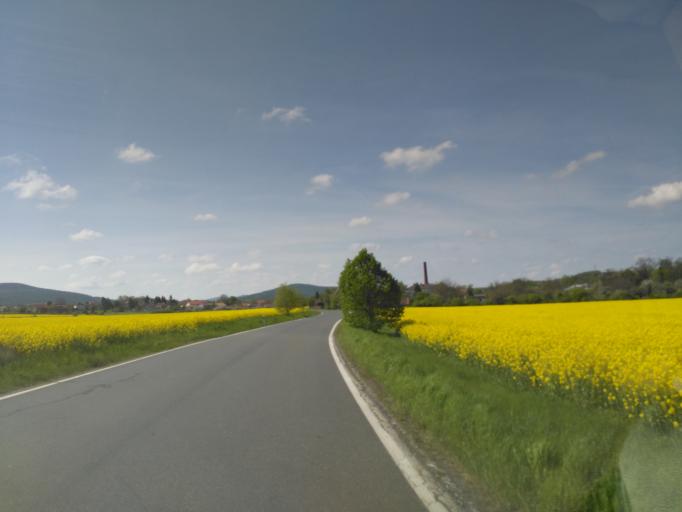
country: CZ
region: Central Bohemia
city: Lochovice
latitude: 49.8598
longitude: 13.9893
